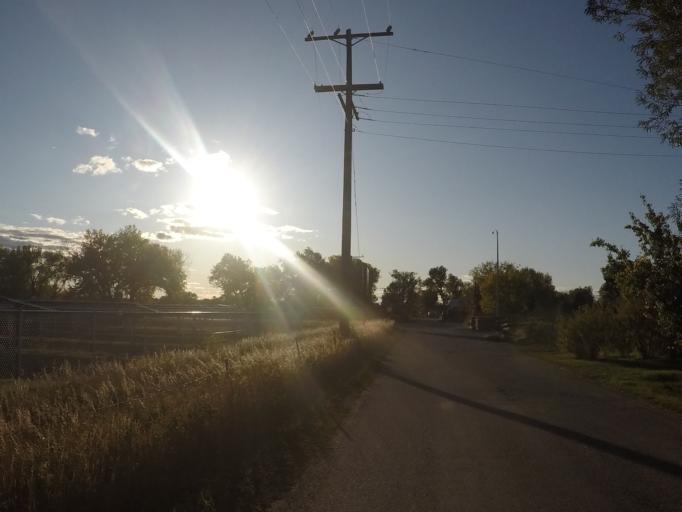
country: US
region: Montana
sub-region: Golden Valley County
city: Ryegate
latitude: 46.2926
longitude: -108.9368
